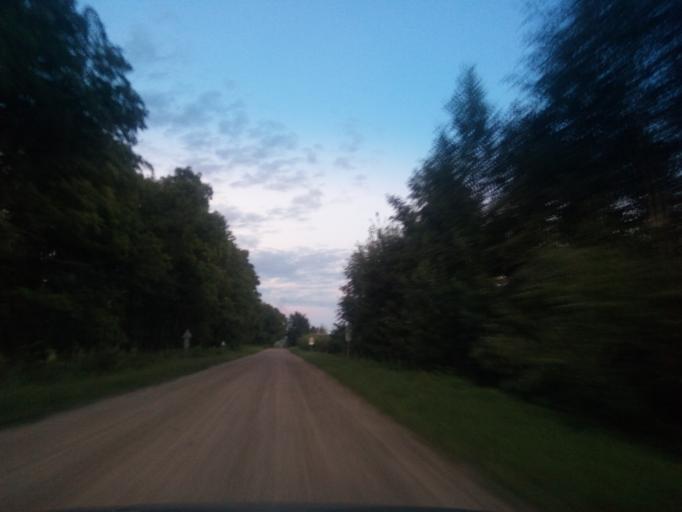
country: BY
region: Vitebsk
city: Dzisna
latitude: 55.6740
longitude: 28.3134
